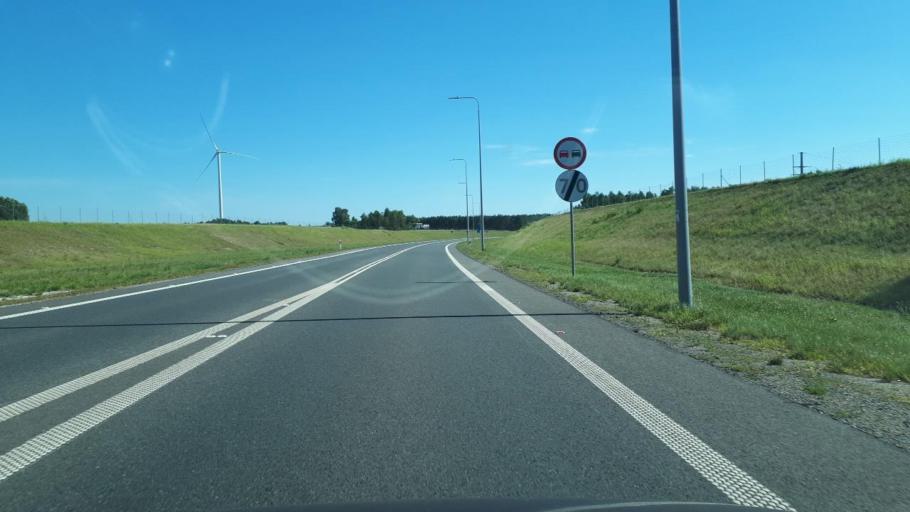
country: PL
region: Greater Poland Voivodeship
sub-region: Powiat kepinski
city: Baranow
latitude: 51.2822
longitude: 18.0277
